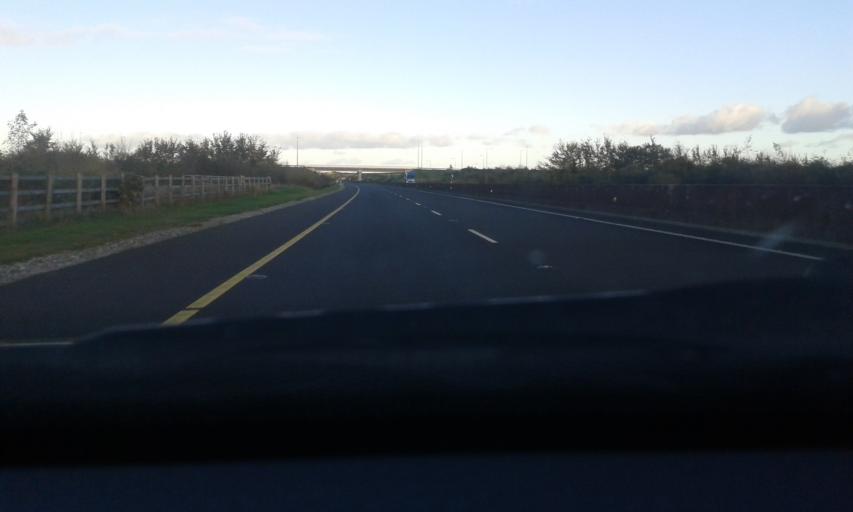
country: IE
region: Munster
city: Thurles
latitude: 52.6634
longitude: -7.7122
